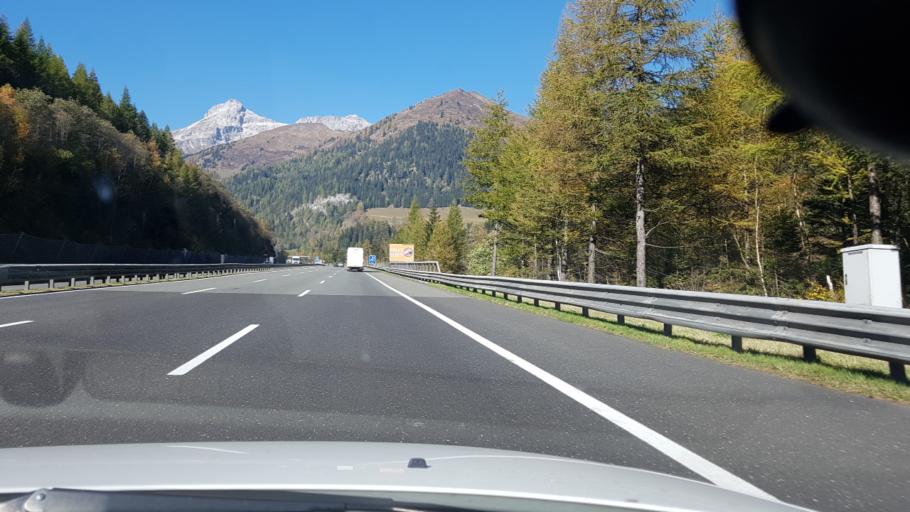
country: AT
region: Salzburg
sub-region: Politischer Bezirk Tamsweg
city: Zederhaus
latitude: 47.1749
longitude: 13.4481
